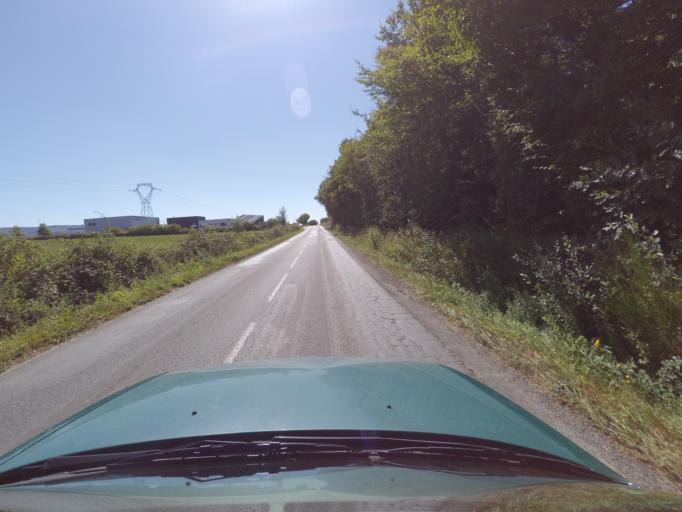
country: FR
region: Pays de la Loire
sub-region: Departement de la Loire-Atlantique
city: Les Sorinieres
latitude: 47.1238
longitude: -1.5101
